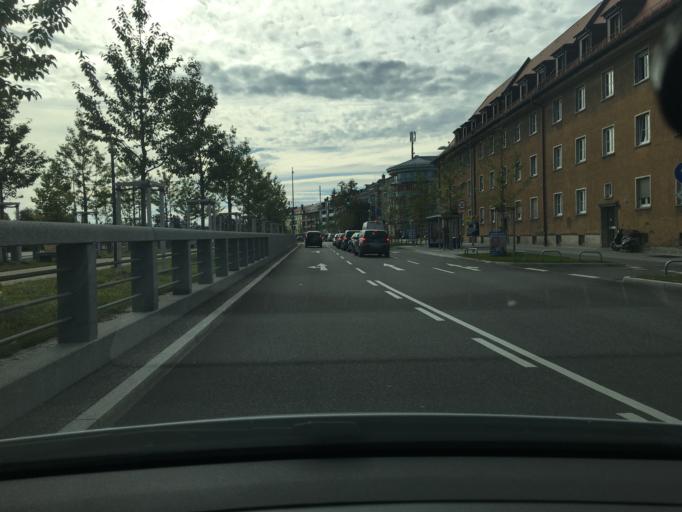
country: DE
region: Bavaria
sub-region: Upper Bavaria
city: Pullach im Isartal
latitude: 48.1142
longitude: 11.5168
